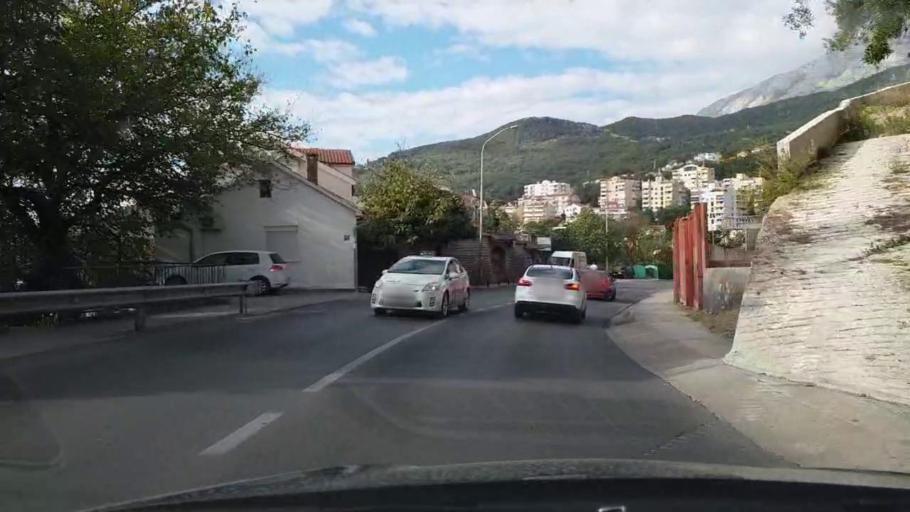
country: ME
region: Herceg Novi
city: Herceg-Novi
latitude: 42.4561
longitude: 18.5273
